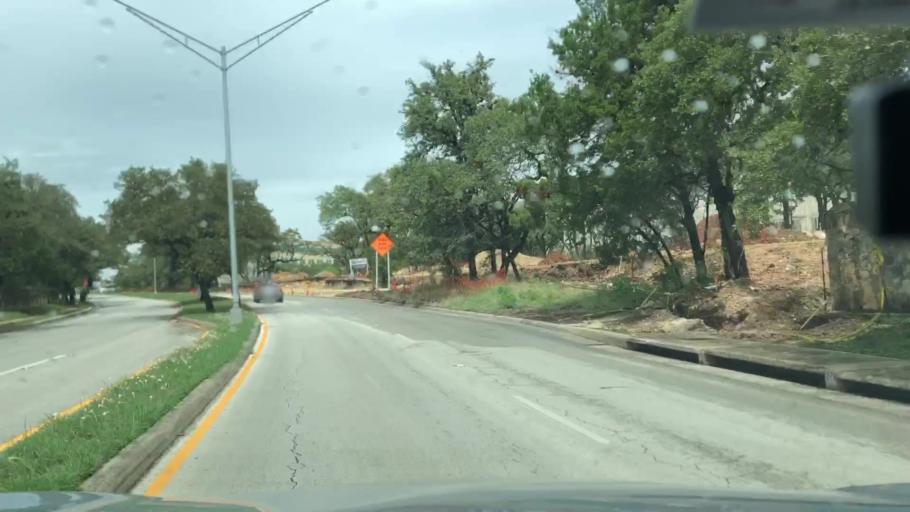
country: US
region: Texas
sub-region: Bexar County
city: Shavano Park
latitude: 29.5993
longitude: -98.5333
